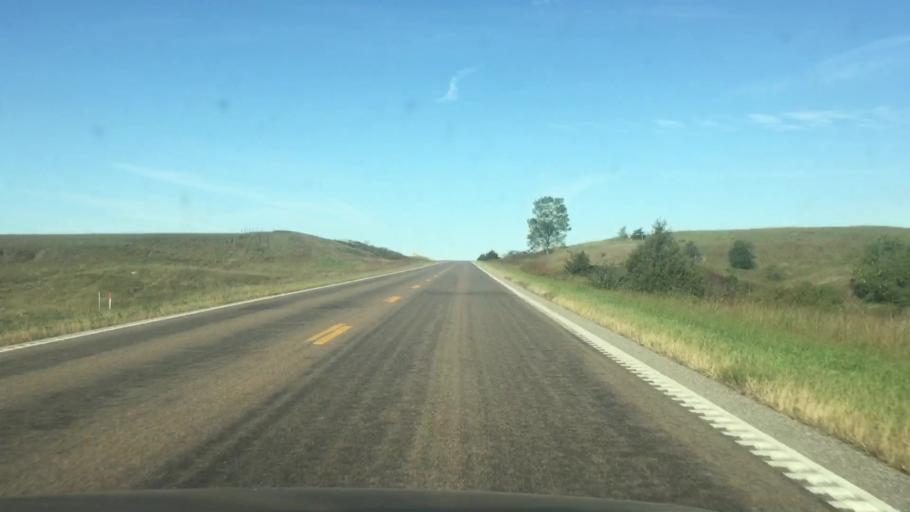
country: US
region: Nebraska
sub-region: Thayer County
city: Hebron
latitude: 40.1473
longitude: -97.5251
